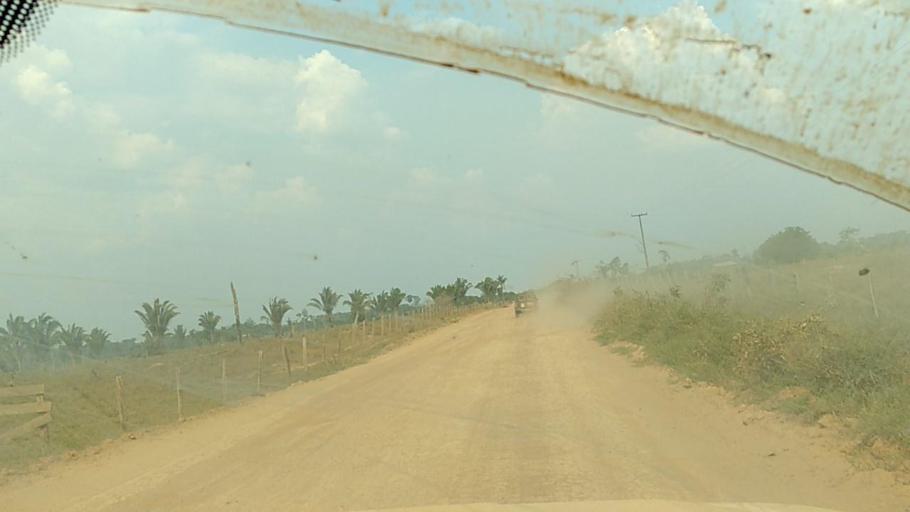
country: BR
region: Rondonia
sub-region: Porto Velho
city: Porto Velho
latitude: -8.6833
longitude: -63.2383
